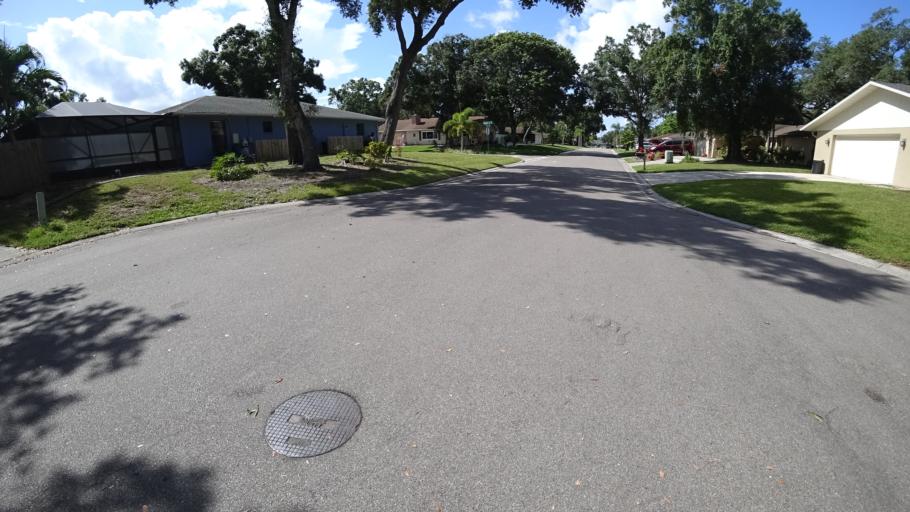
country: US
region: Florida
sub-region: Sarasota County
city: Desoto Lakes
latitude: 27.3916
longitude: -82.4985
